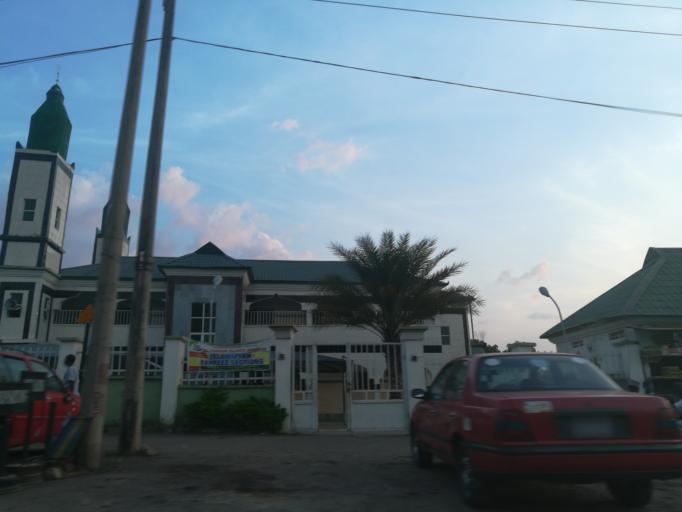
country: NG
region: Abuja Federal Capital Territory
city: Abuja
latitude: 9.0785
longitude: 7.3907
